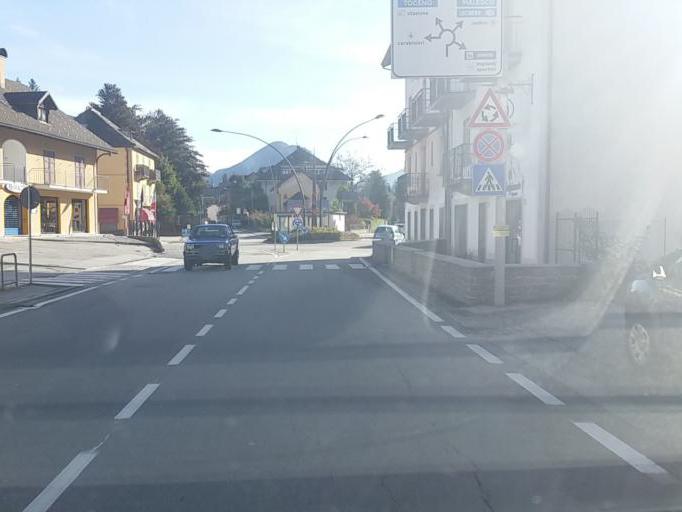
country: IT
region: Piedmont
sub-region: Provincia Verbano-Cusio-Ossola
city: Santa Maria Maggiore
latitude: 46.1339
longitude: 8.4589
